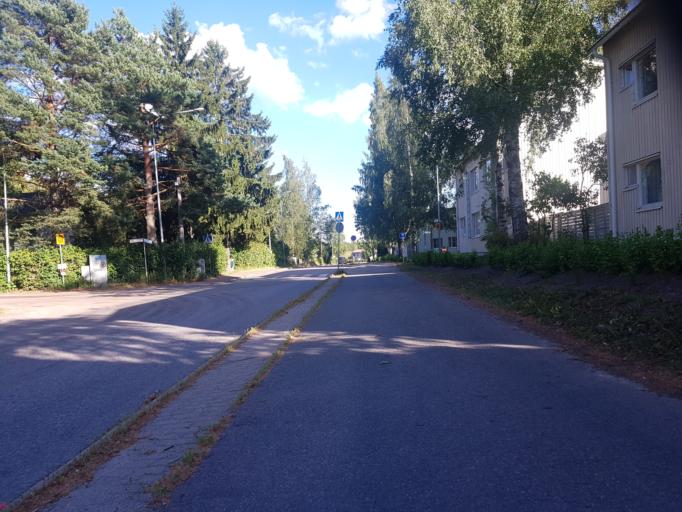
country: FI
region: Uusimaa
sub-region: Helsinki
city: Vantaa
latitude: 60.2706
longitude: 25.0070
